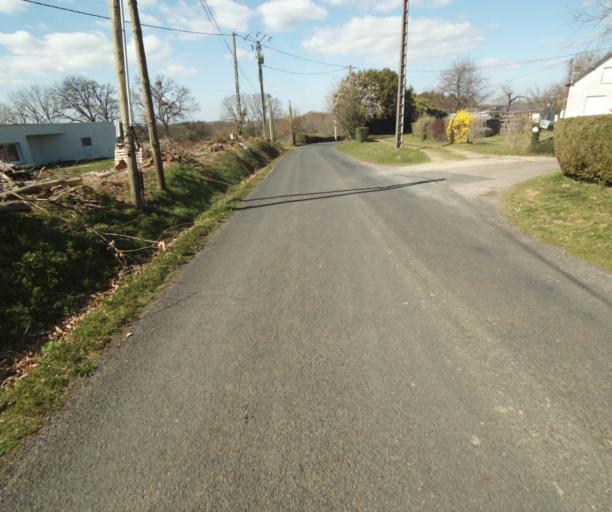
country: FR
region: Limousin
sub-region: Departement de la Correze
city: Saint-Mexant
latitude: 45.2942
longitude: 1.6494
